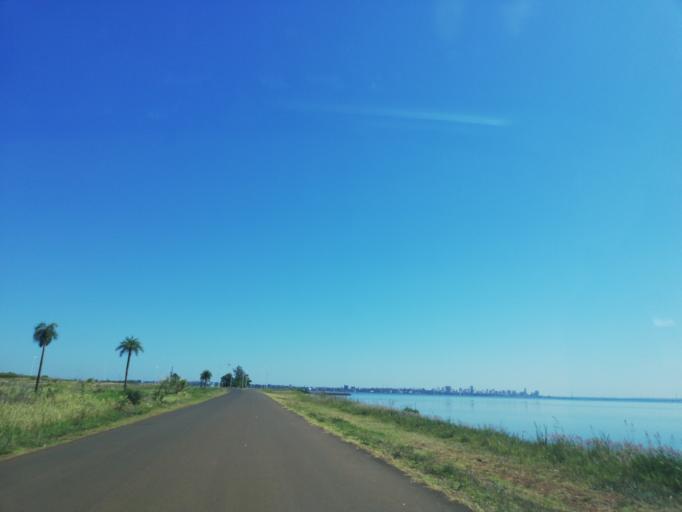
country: AR
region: Misiones
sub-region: Departamento de Capital
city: Posadas
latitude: -27.4249
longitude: -55.8713
